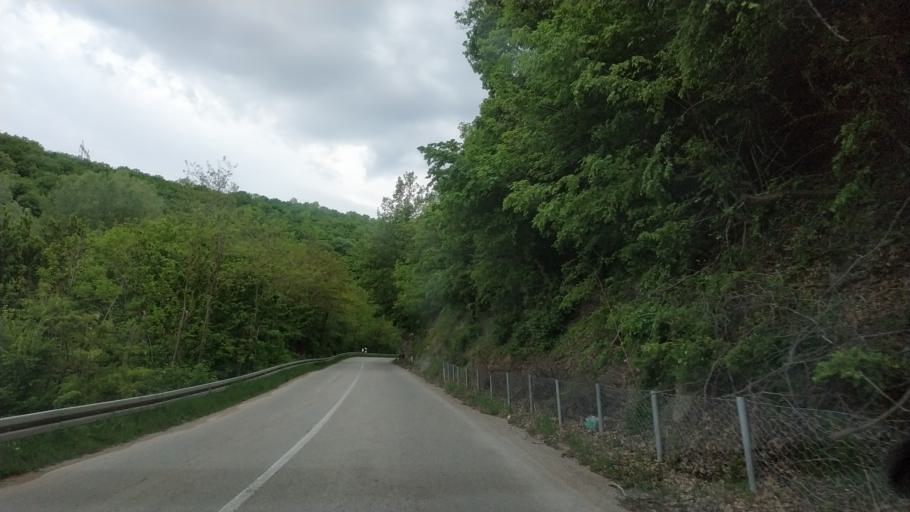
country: RS
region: Central Serbia
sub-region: Nisavski Okrug
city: Aleksinac
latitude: 43.6228
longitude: 21.6982
